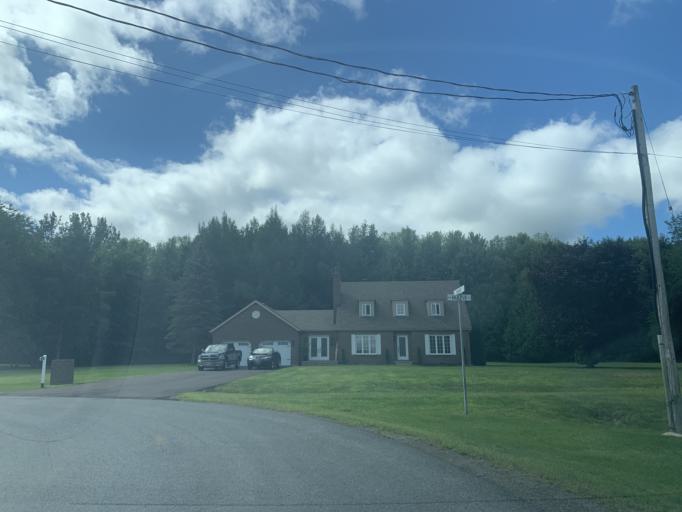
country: CA
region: Ontario
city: Hawkesbury
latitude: 45.6010
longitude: -74.5800
